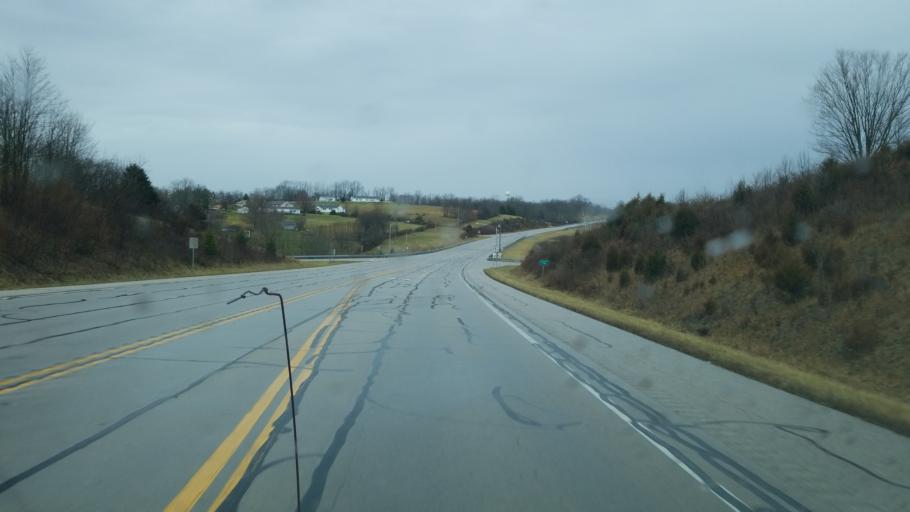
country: US
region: Ohio
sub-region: Adams County
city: Manchester
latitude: 38.5676
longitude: -83.6426
